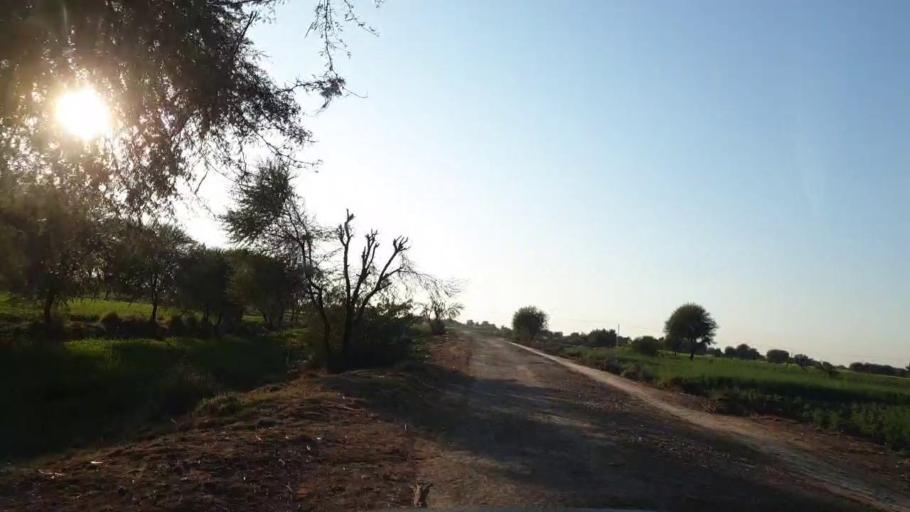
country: PK
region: Sindh
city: Jhol
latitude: 25.8808
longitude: 68.9105
